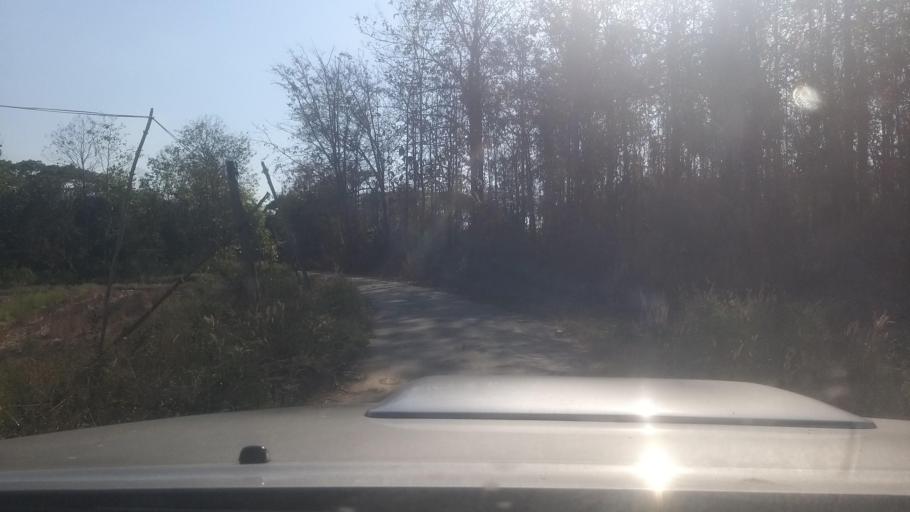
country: TH
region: Phrae
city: Phrae
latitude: 18.2677
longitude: 99.9856
